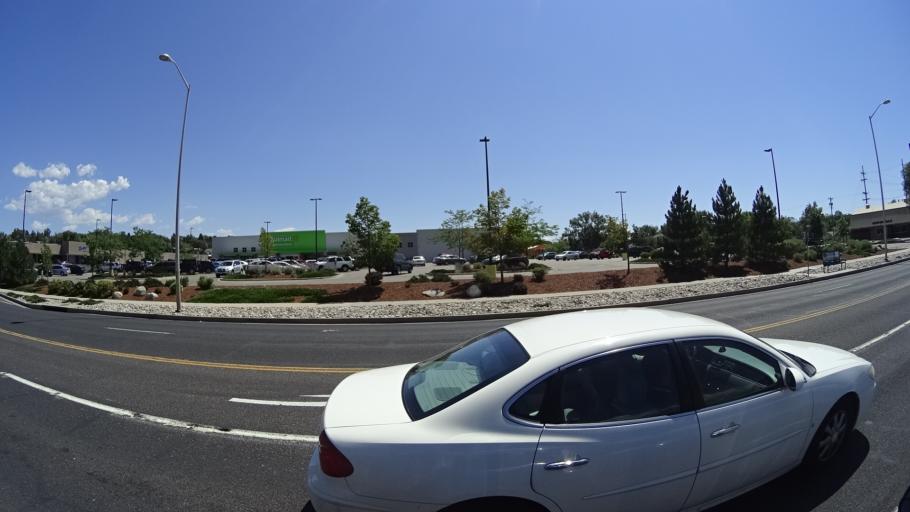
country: US
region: Colorado
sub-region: El Paso County
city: Colorado Springs
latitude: 38.8574
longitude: -104.7943
